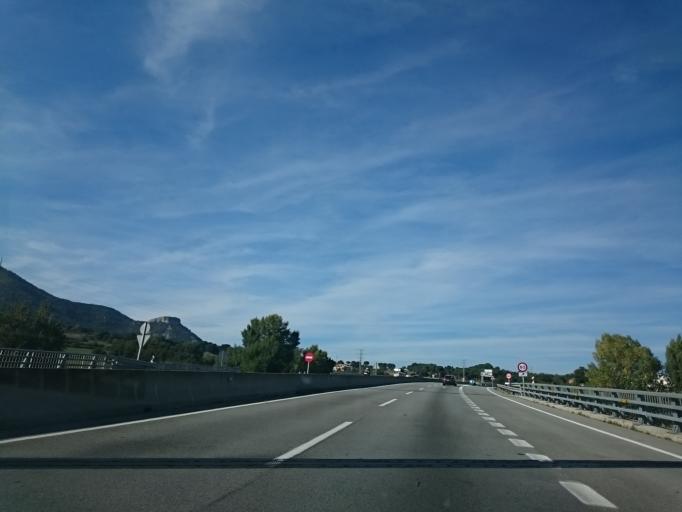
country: ES
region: Catalonia
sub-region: Provincia de Barcelona
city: Centelles
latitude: 41.8076
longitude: 2.2258
